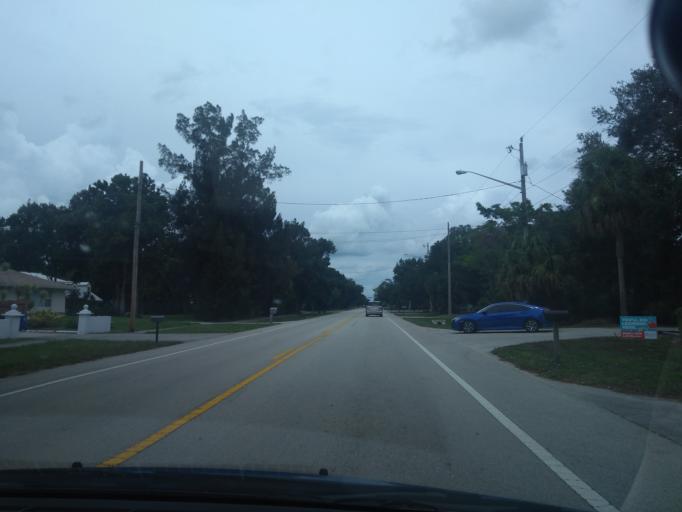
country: US
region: Florida
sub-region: Indian River County
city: Vero Beach South
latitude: 27.6280
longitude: -80.4138
